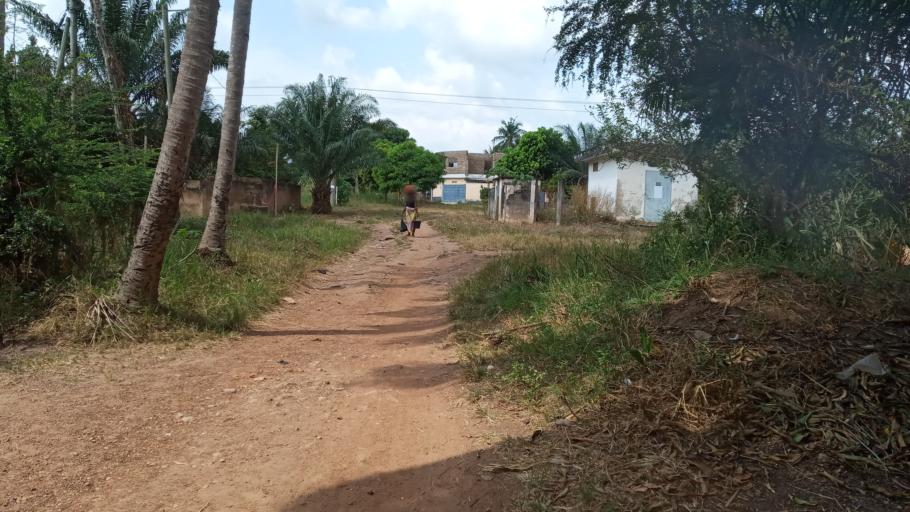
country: TG
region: Plateaux
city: Kpalime
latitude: 6.9193
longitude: 0.6314
